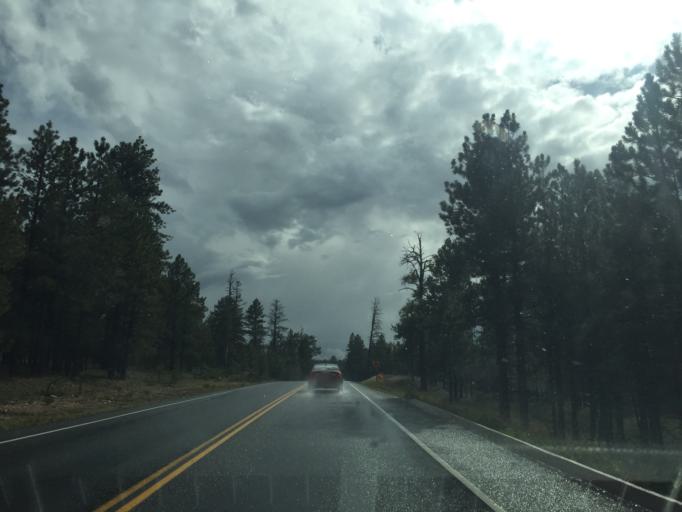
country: US
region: Utah
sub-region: Garfield County
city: Panguitch
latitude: 37.6449
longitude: -112.1664
